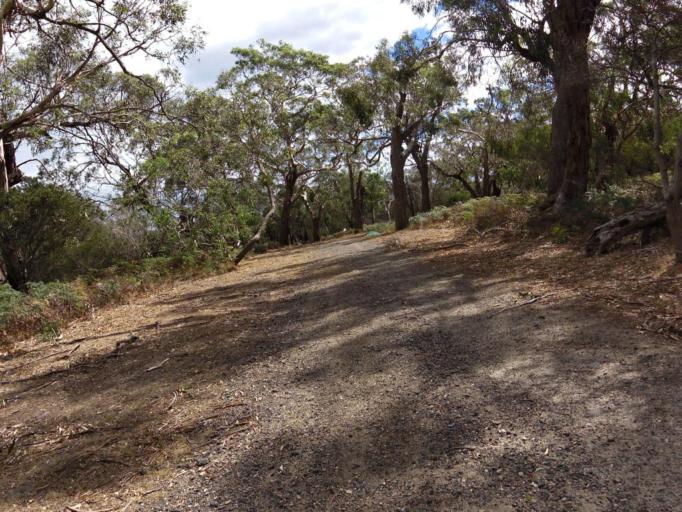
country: AU
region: Victoria
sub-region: Mornington Peninsula
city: Mount Martha
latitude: -38.2660
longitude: 145.0457
